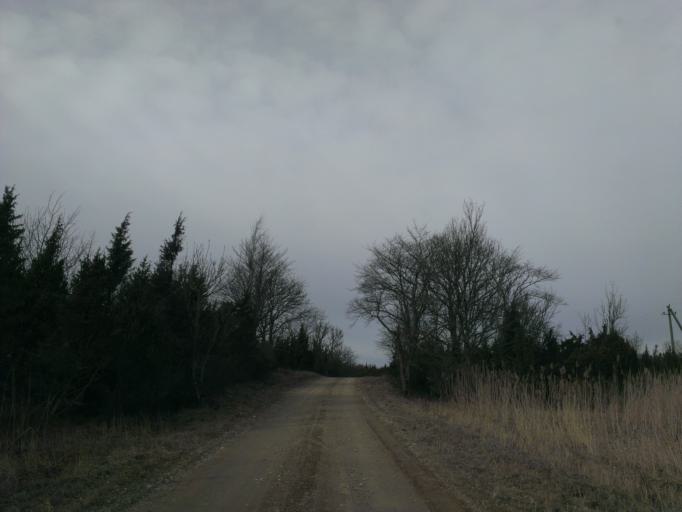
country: EE
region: Laeaene
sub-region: Lihula vald
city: Lihula
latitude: 58.5652
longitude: 23.5475
